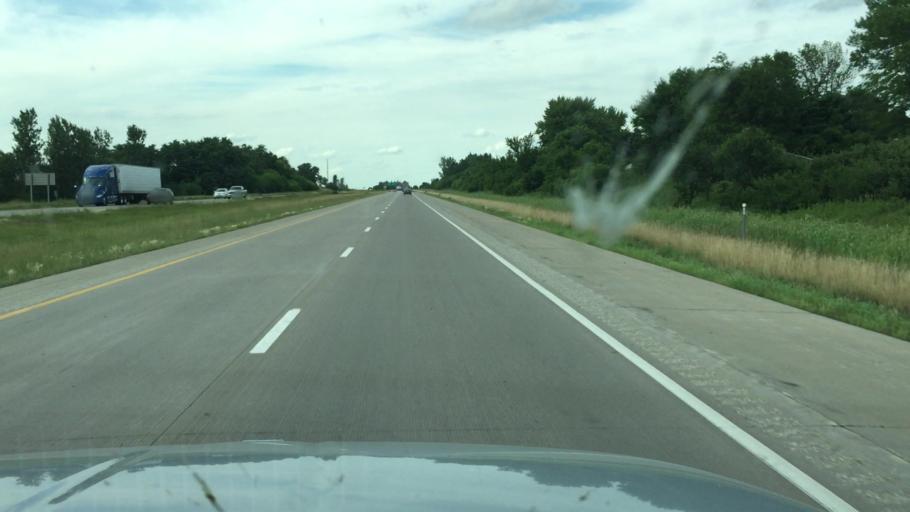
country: US
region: Iowa
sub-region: Scott County
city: Walcott
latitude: 41.5755
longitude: -90.6774
